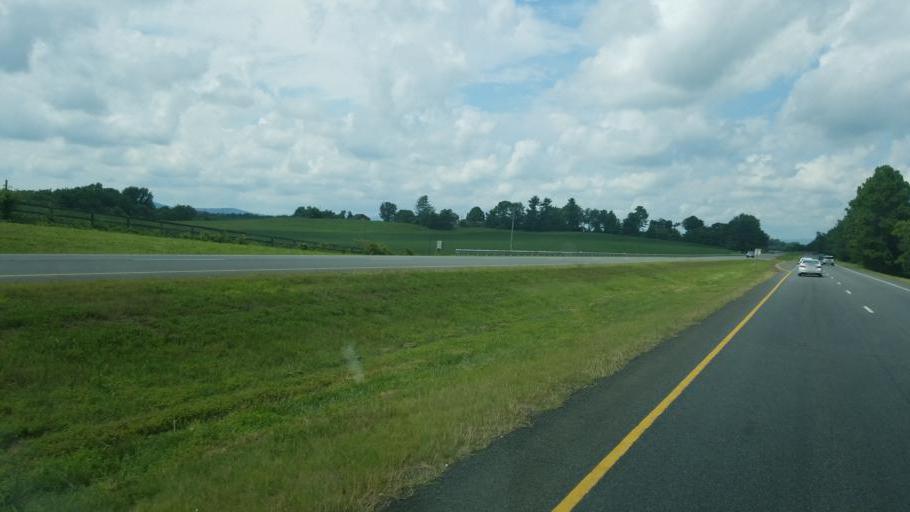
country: US
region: Virginia
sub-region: Fauquier County
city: Marshall
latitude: 38.8373
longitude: -77.8234
